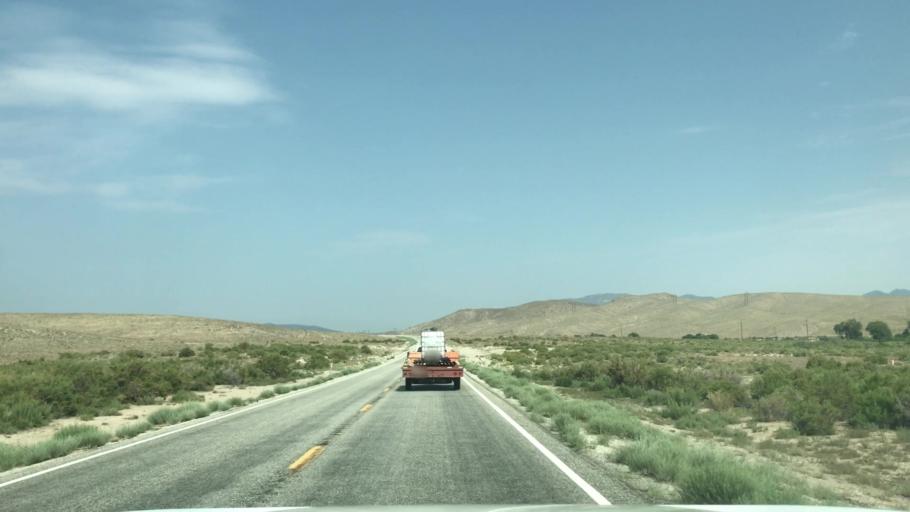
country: US
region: Nevada
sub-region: White Pine County
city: McGill
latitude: 39.0816
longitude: -114.1948
